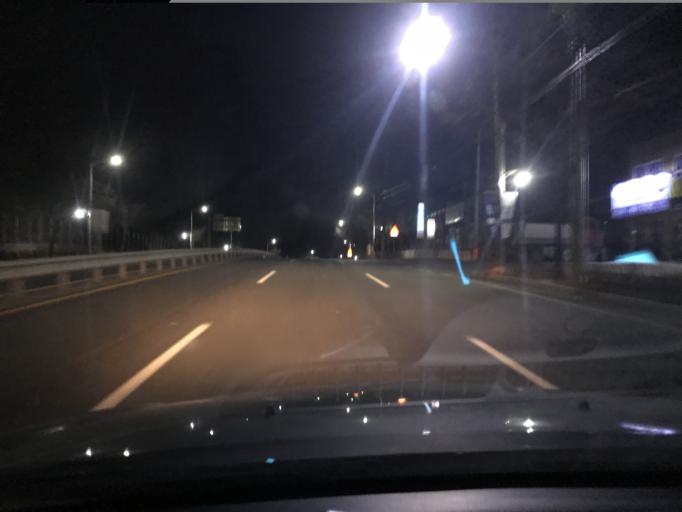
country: KR
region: Daegu
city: Hwawon
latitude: 35.6995
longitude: 128.4386
